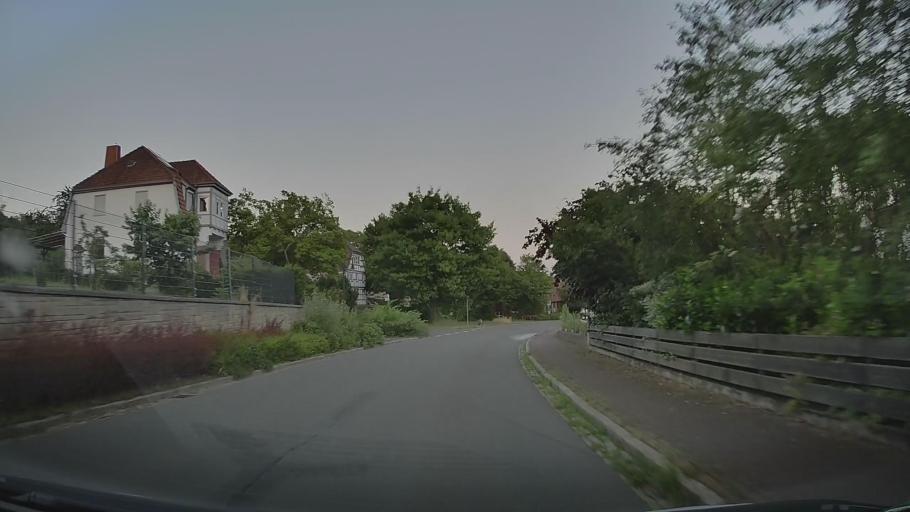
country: DE
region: Lower Saxony
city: Aerzen
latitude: 52.0181
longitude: 9.3067
